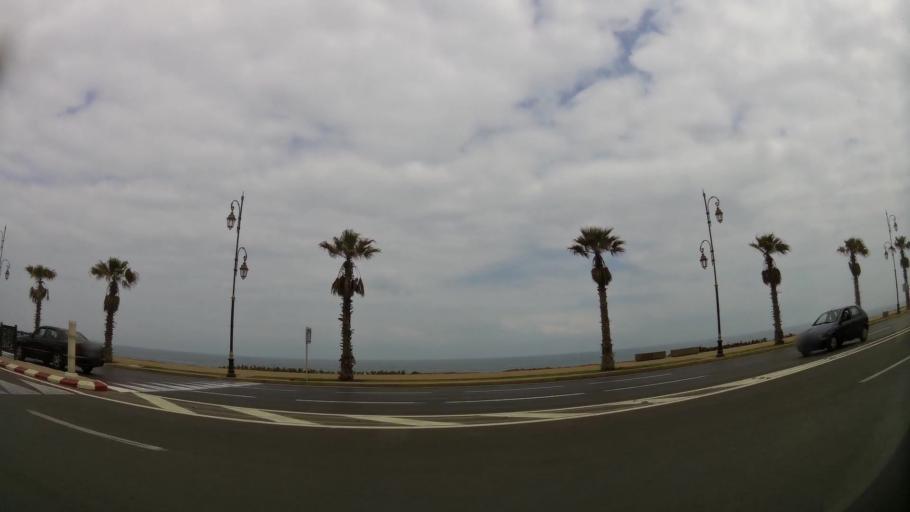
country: MA
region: Rabat-Sale-Zemmour-Zaer
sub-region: Rabat
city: Rabat
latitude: 33.9920
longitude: -6.8840
